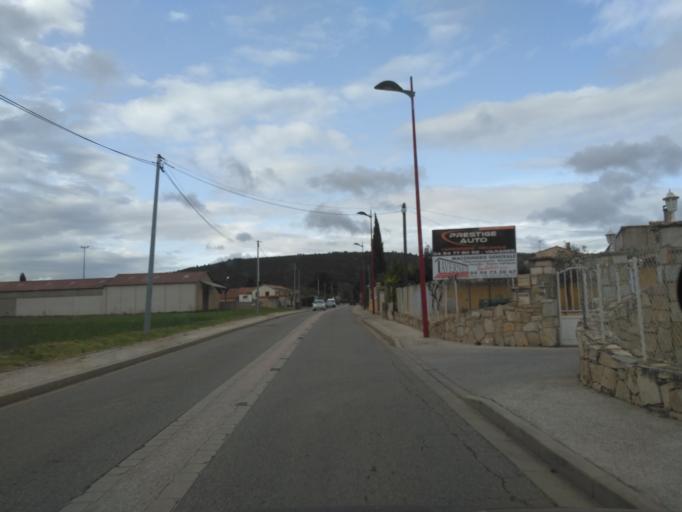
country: FR
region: Provence-Alpes-Cote d'Azur
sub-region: Departement du Var
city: Barjols
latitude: 43.5895
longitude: 6.0132
